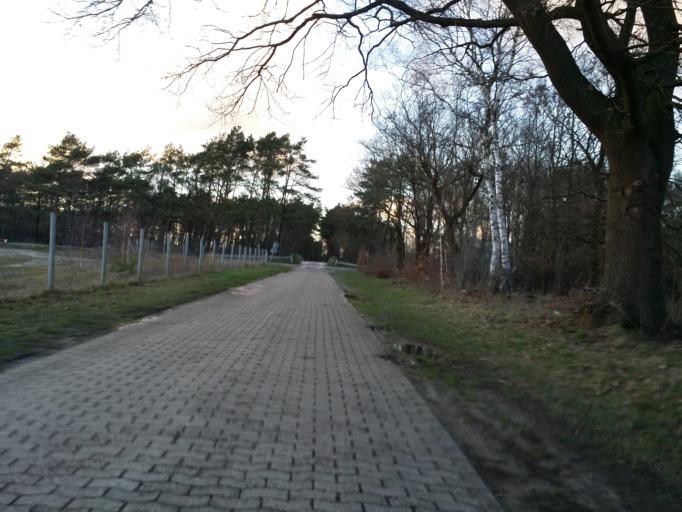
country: DE
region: Lower Saxony
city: Gross Ippener
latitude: 52.9648
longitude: 8.6004
